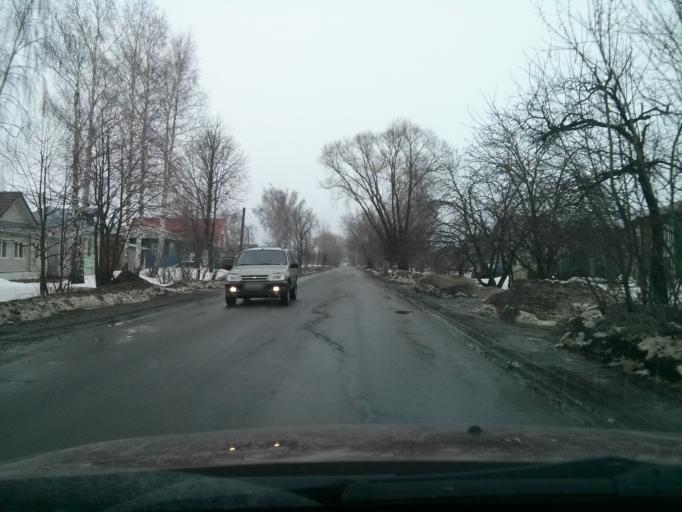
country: RU
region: Vladimir
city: Murom
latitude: 55.5400
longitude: 42.0252
